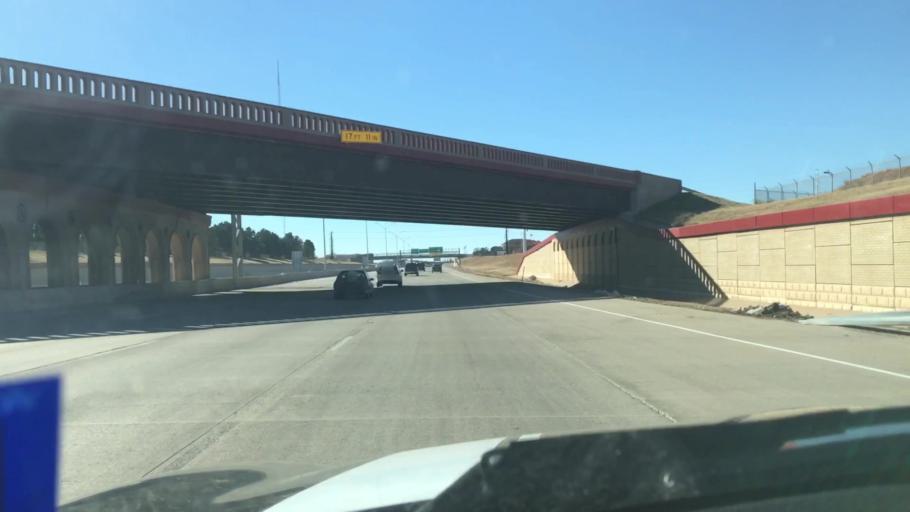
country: US
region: Texas
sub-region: Lubbock County
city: Lubbock
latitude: 33.5879
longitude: -101.8841
